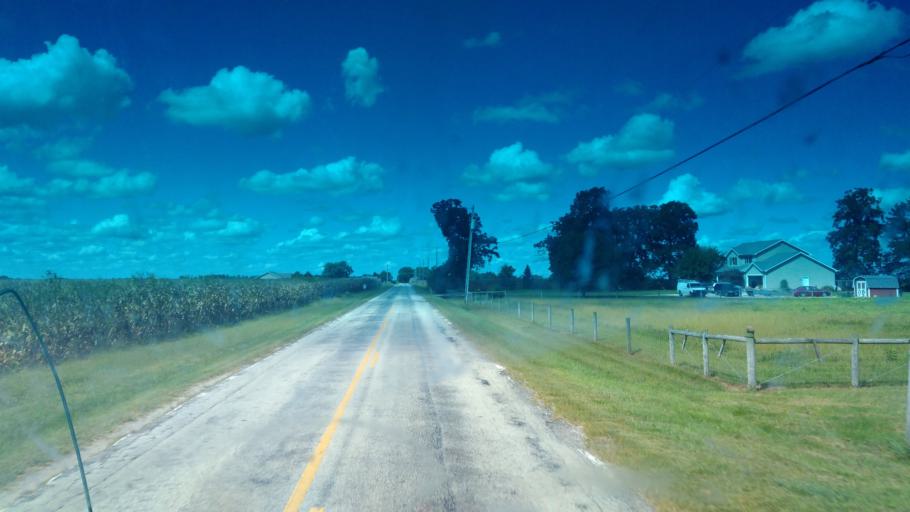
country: US
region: Ohio
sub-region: Madison County
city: West Jefferson
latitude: 40.0079
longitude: -83.3586
